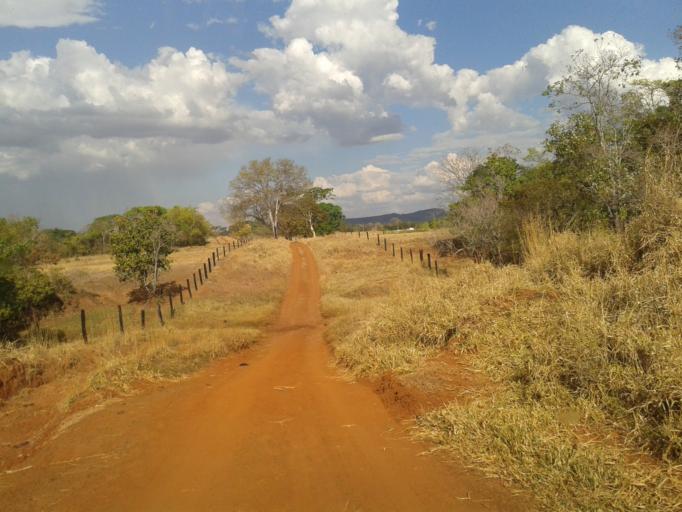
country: BR
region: Minas Gerais
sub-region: Santa Vitoria
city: Santa Vitoria
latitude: -19.1675
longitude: -50.0007
